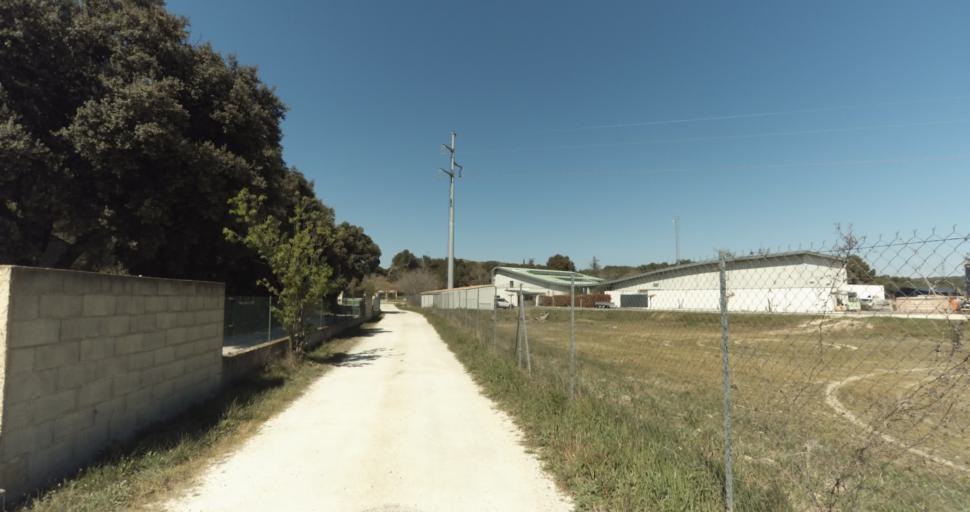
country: FR
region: Provence-Alpes-Cote d'Azur
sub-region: Departement des Bouches-du-Rhone
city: Pelissanne
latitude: 43.6351
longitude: 5.1705
